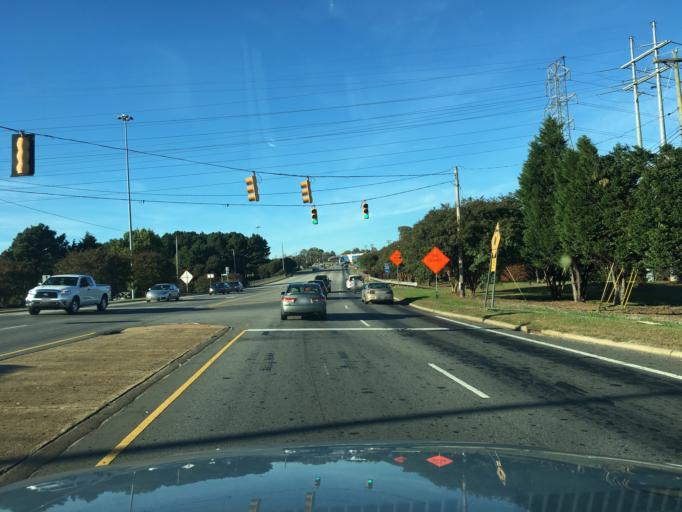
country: US
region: North Carolina
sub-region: Catawba County
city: Hickory
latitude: 35.7119
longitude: -81.3125
